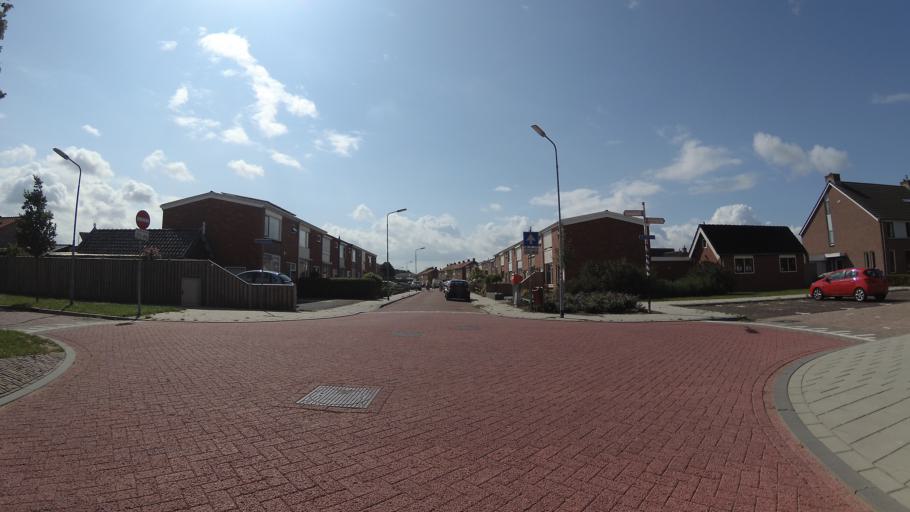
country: NL
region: Zeeland
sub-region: Gemeente Middelburg
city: Middelburg
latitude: 51.5275
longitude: 3.6040
